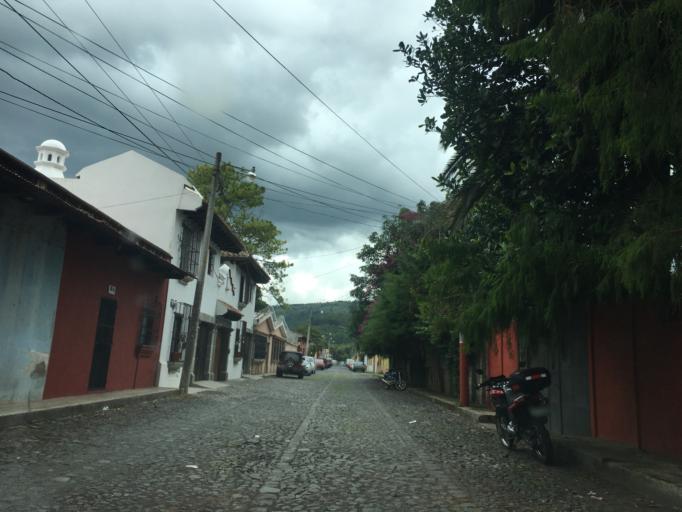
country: GT
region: Sacatepequez
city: Antigua Guatemala
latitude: 14.5421
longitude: -90.7440
